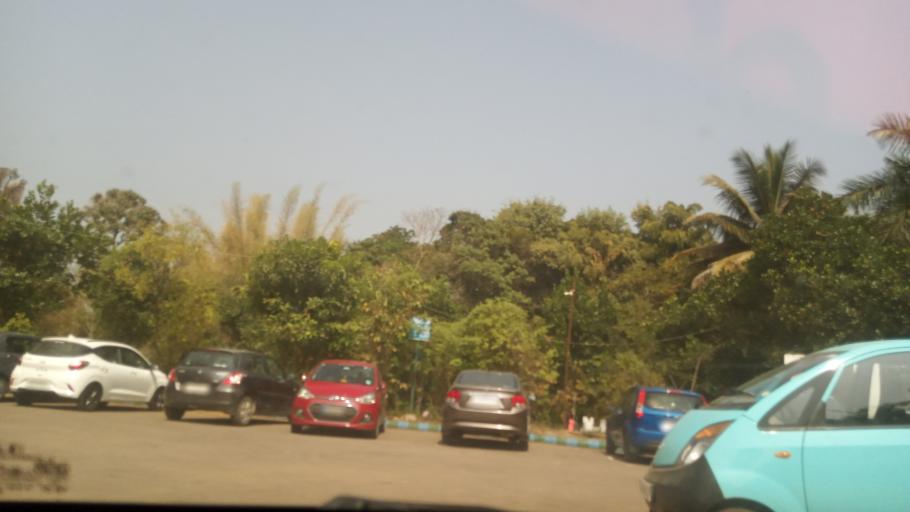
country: IN
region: Karnataka
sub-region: Mandya
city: Shrirangapattana
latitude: 12.4238
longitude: 76.6565
